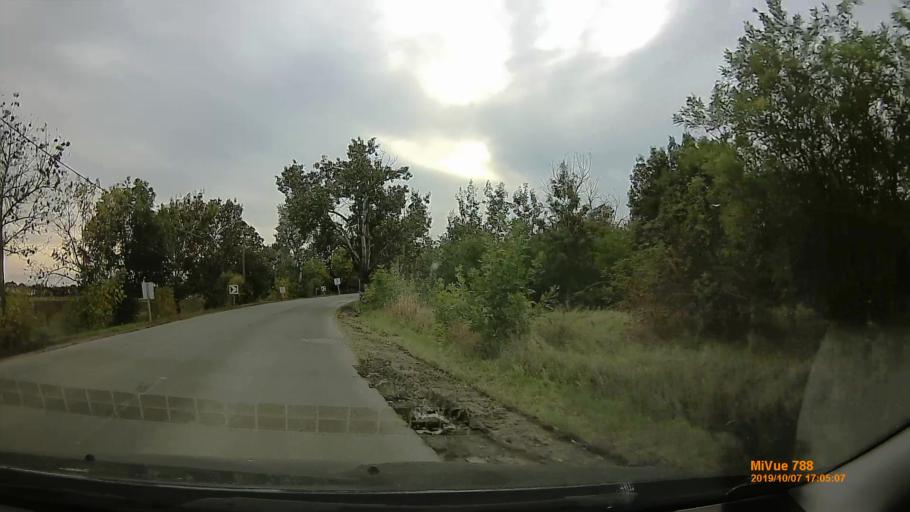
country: HU
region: Bekes
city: Szarvas
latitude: 46.8274
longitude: 20.5412
